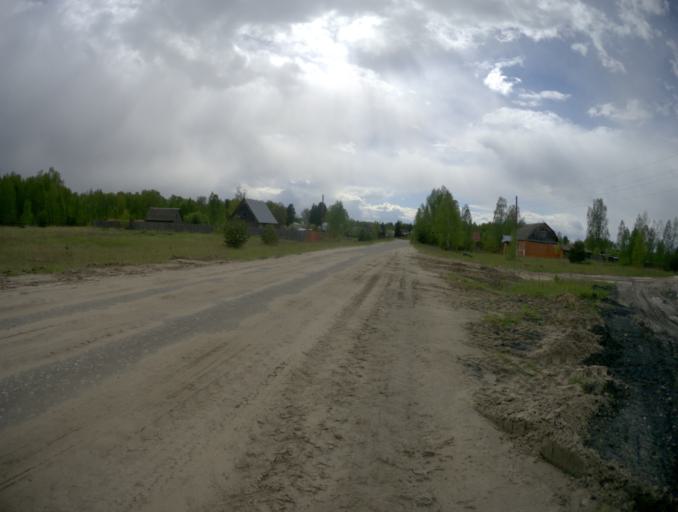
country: RU
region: Vladimir
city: Velikodvorskiy
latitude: 55.2274
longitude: 40.6451
